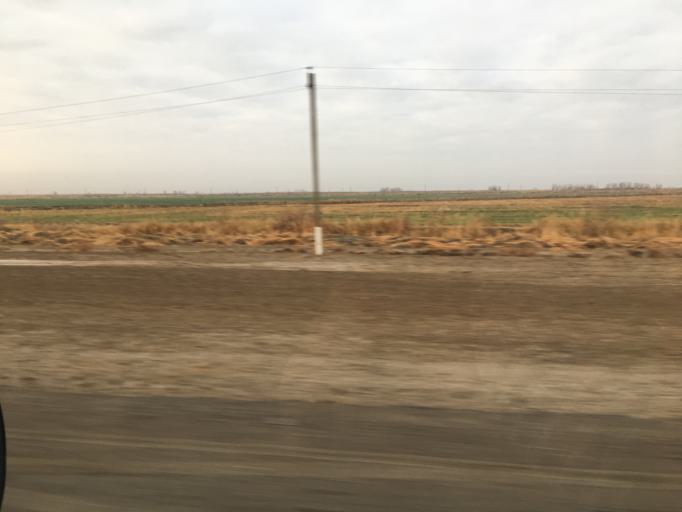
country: TM
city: Murgab
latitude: 37.4796
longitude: 62.0069
